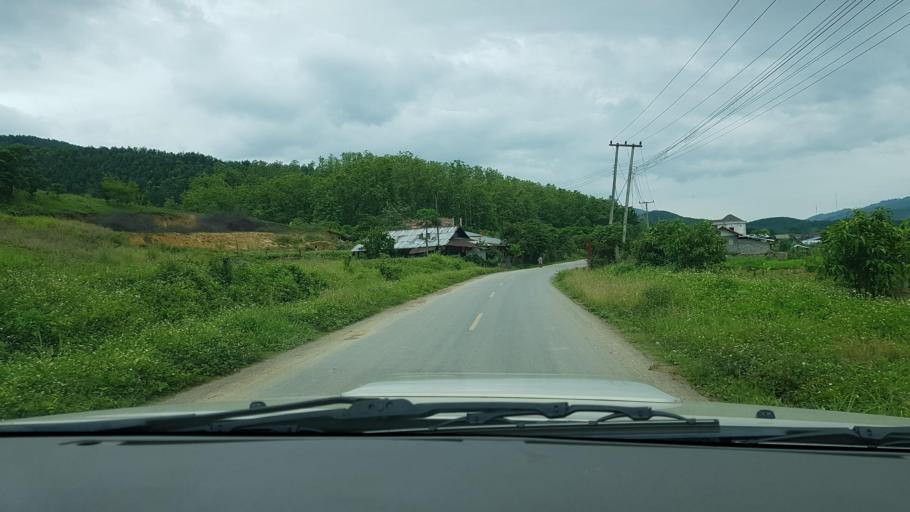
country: LA
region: Loungnamtha
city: Muang Nale
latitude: 20.2598
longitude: 101.5918
